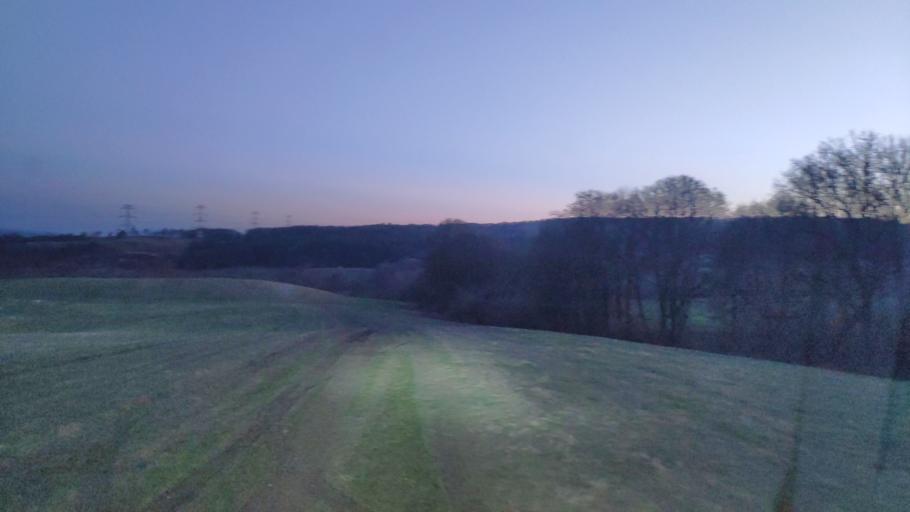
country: SK
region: Kosicky
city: Kosice
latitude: 48.8252
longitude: 21.2647
